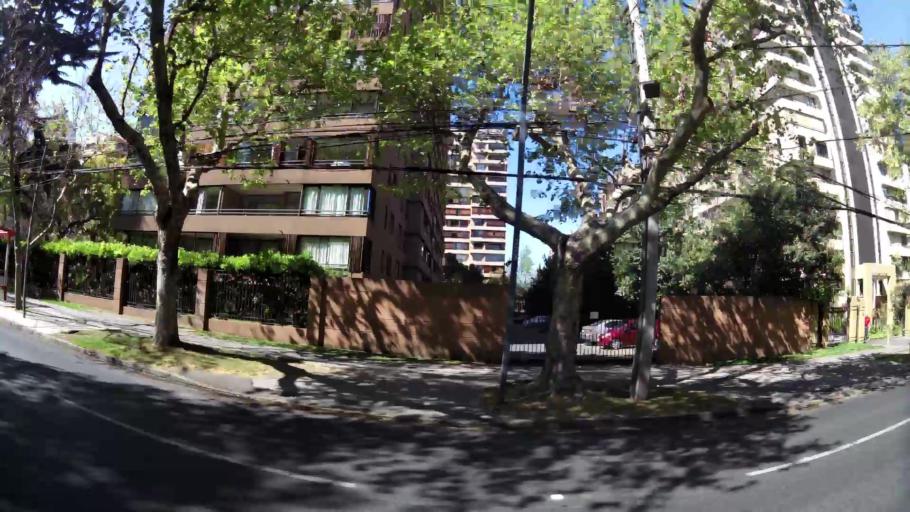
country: CL
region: Santiago Metropolitan
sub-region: Provincia de Santiago
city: Villa Presidente Frei, Nunoa, Santiago, Chile
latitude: -33.4178
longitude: -70.5687
